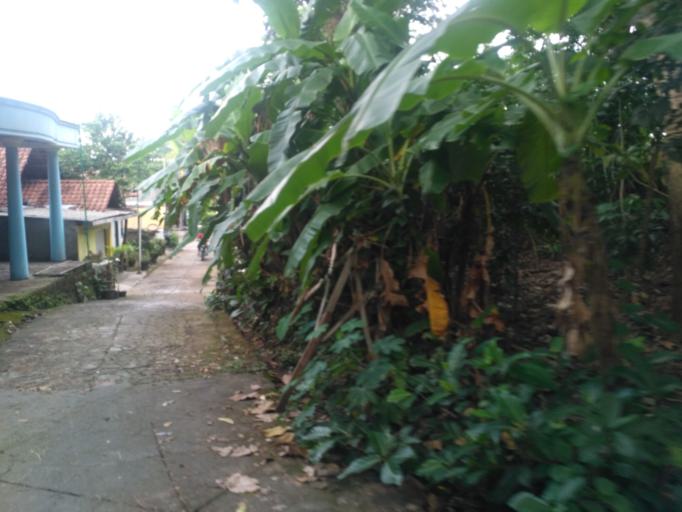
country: ID
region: Daerah Istimewa Yogyakarta
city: Yogyakarta
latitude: -7.7645
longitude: 110.3526
